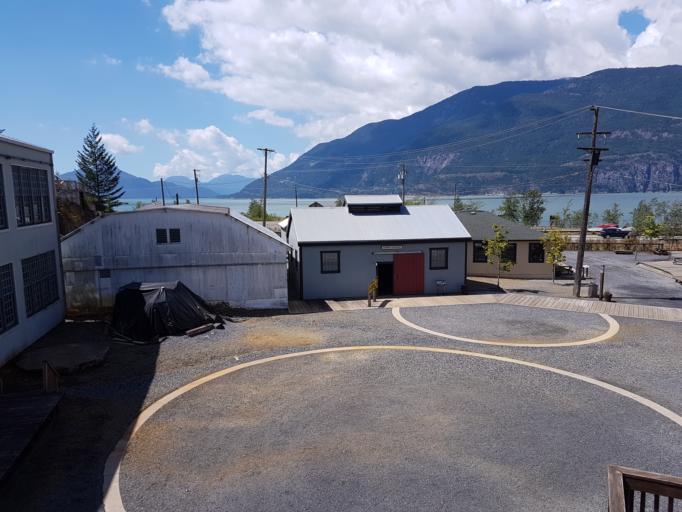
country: CA
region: British Columbia
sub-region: Greater Vancouver Regional District
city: Lions Bay
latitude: 49.6229
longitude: -123.2042
